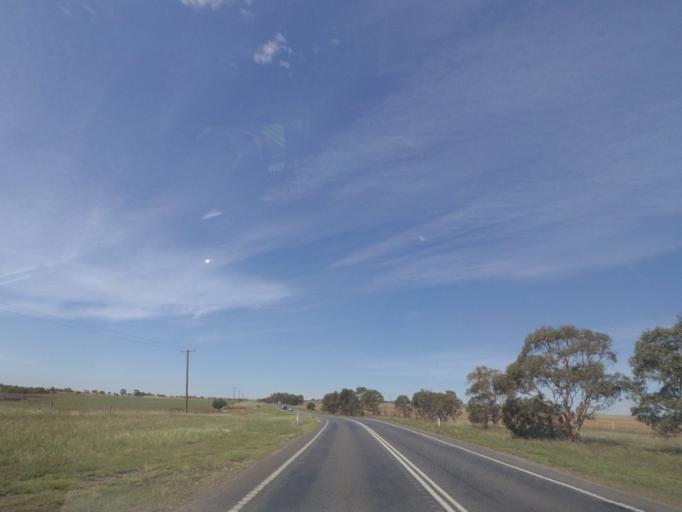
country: AU
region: Victoria
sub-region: Moorabool
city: Bacchus Marsh
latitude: -37.7550
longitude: 144.4422
